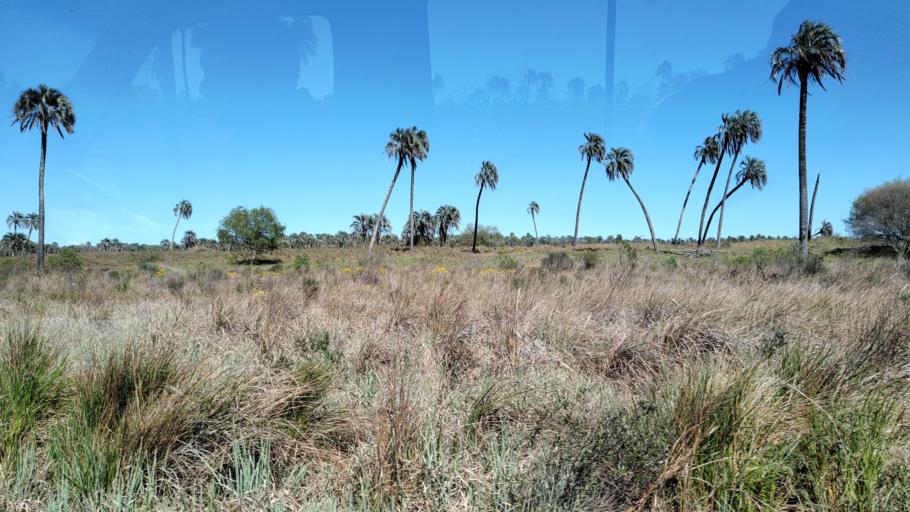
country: AR
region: Entre Rios
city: Ubajay
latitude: -31.8832
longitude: -58.2368
